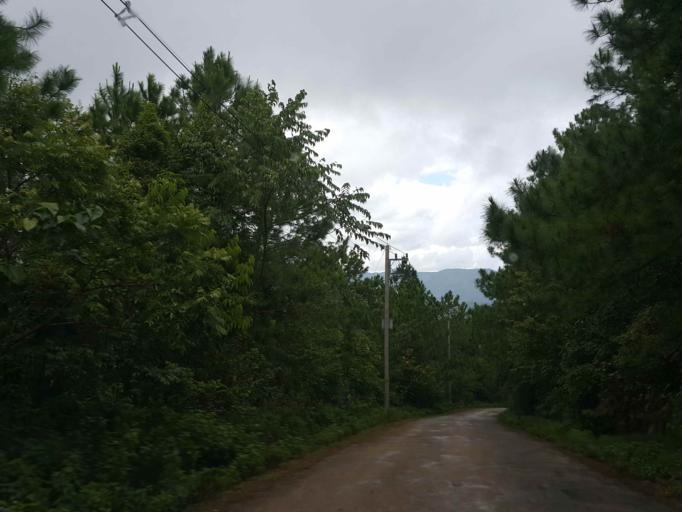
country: TH
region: Chiang Mai
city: Mae Chaem
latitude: 18.5119
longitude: 98.5263
